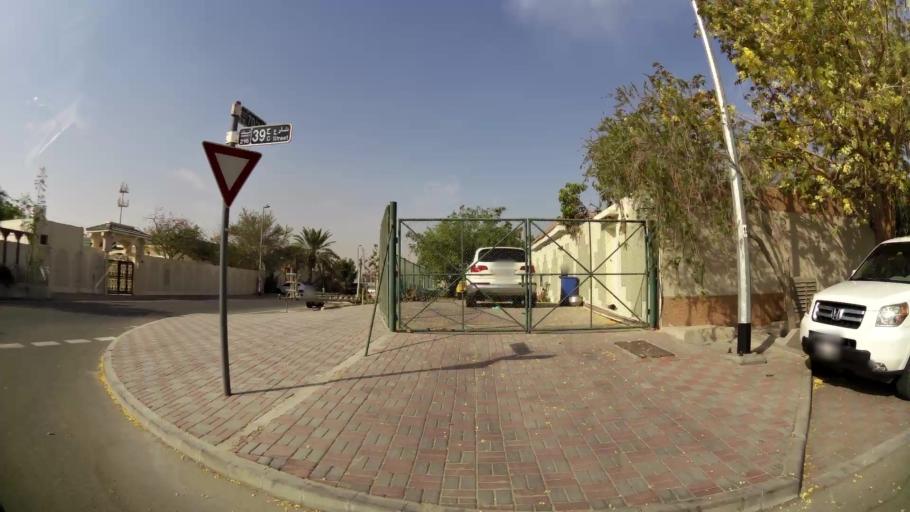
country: AE
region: Ash Shariqah
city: Sharjah
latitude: 25.2220
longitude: 55.4011
